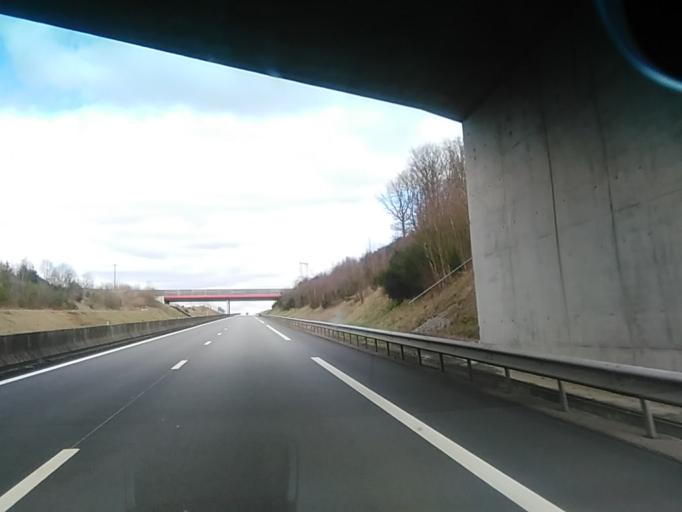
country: FR
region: Haute-Normandie
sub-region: Departement de l'Eure
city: Bourg-Achard
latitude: 49.2855
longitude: 0.7820
